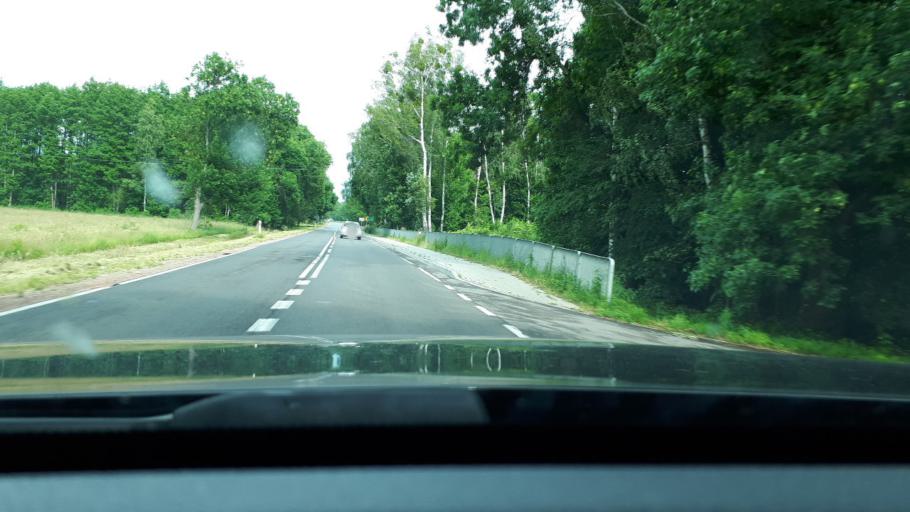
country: PL
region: Masovian Voivodeship
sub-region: Powiat warszawski zachodni
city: Kampinos
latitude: 52.2696
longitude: 20.4126
